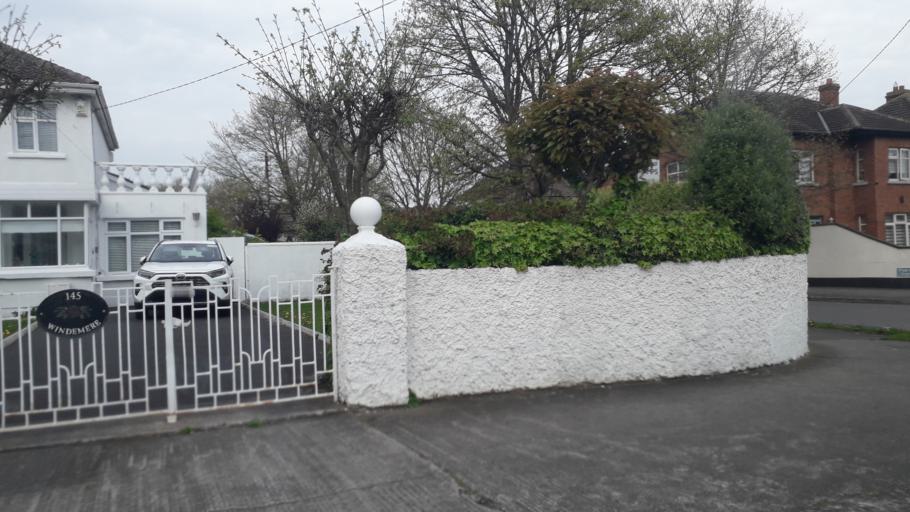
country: IE
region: Leinster
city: Dollymount
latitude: 53.3614
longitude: -6.1889
